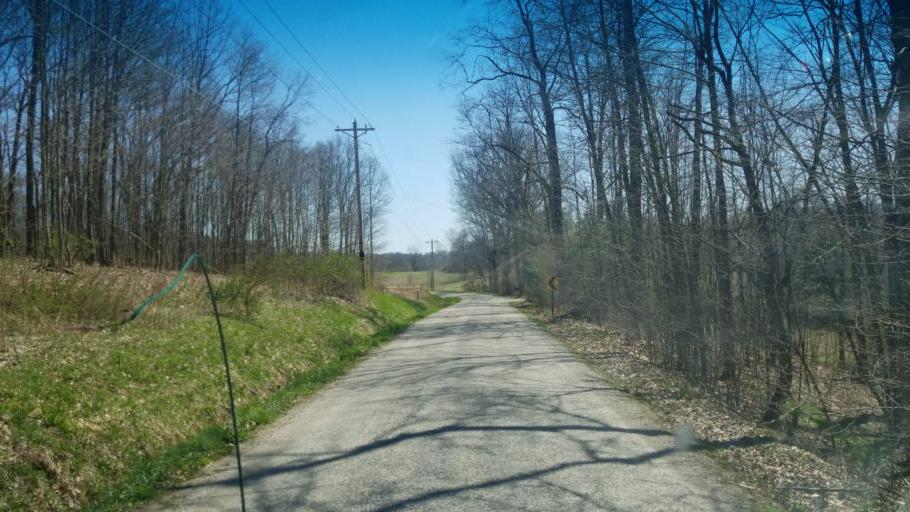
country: US
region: Ohio
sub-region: Ashland County
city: Ashland
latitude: 40.8450
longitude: -82.3877
